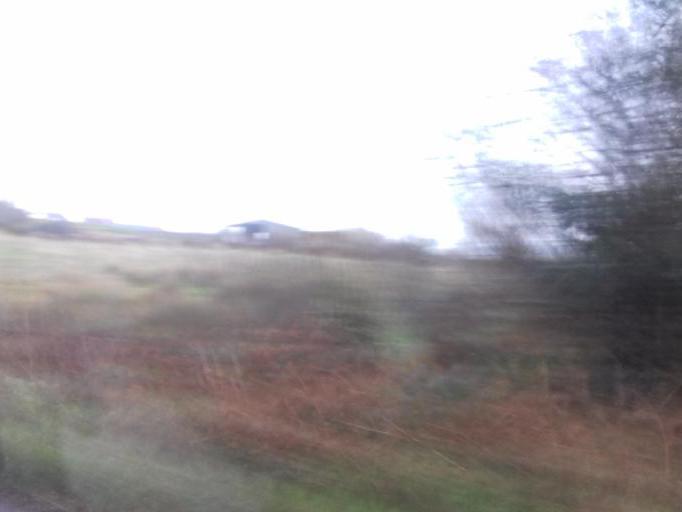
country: IE
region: Ulster
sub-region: County Donegal
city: Buncrana
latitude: 55.1717
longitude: -7.5828
